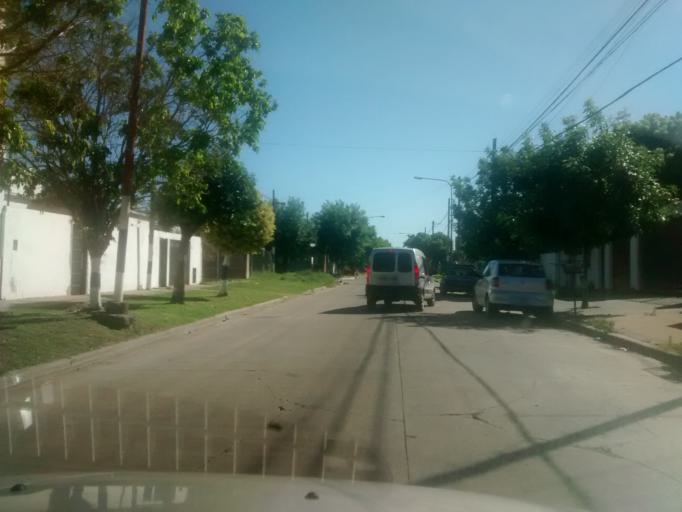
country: AR
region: Buenos Aires
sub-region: Partido de La Plata
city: La Plata
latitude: -34.9406
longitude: -57.9343
